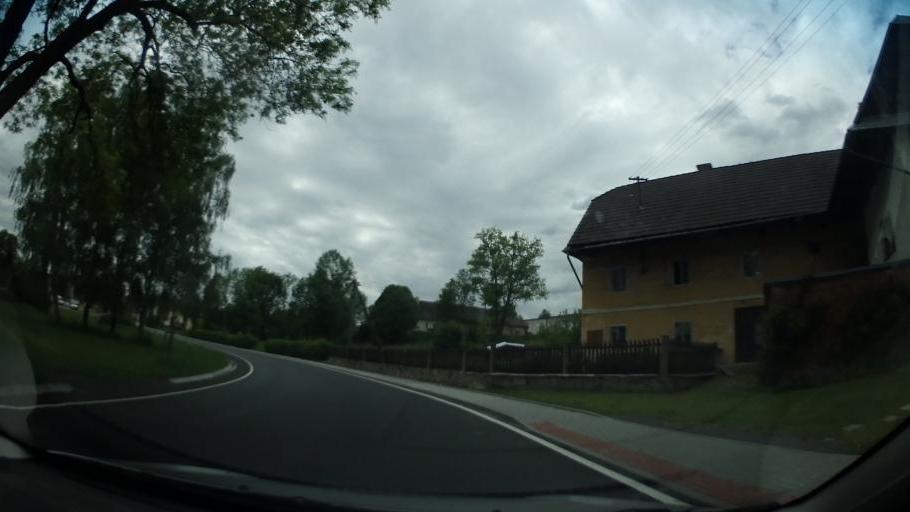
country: CZ
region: Pardubicky
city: Kuncina
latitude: 49.8582
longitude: 16.6944
